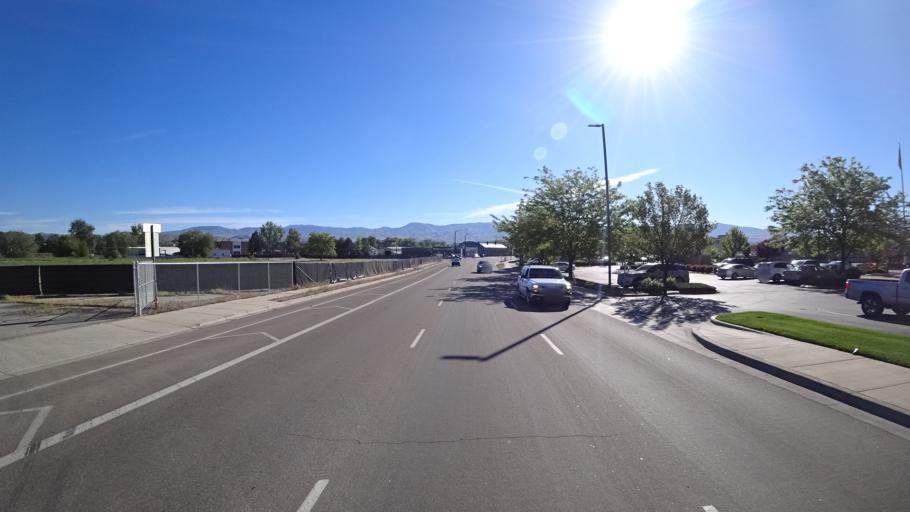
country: US
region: Idaho
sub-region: Ada County
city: Garden City
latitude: 43.6211
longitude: -116.2295
